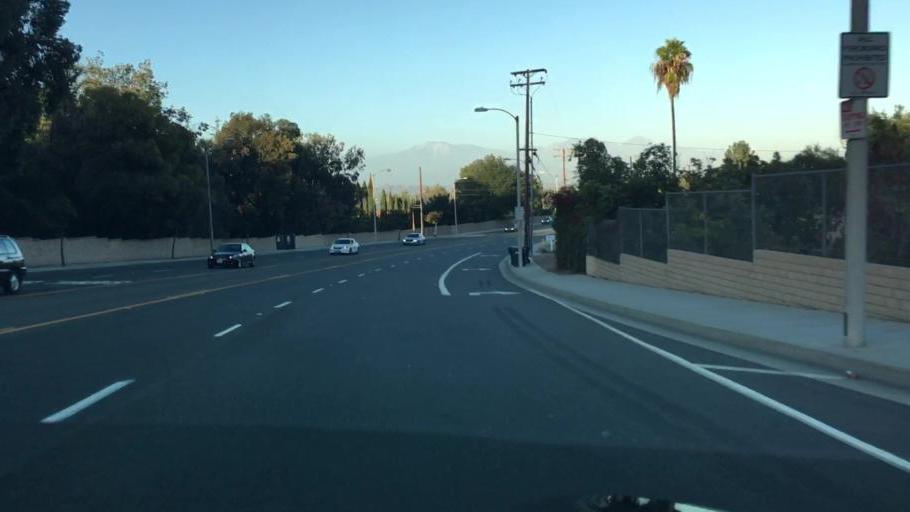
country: US
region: California
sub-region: Los Angeles County
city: Rowland Heights
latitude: 33.9688
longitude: -117.9148
